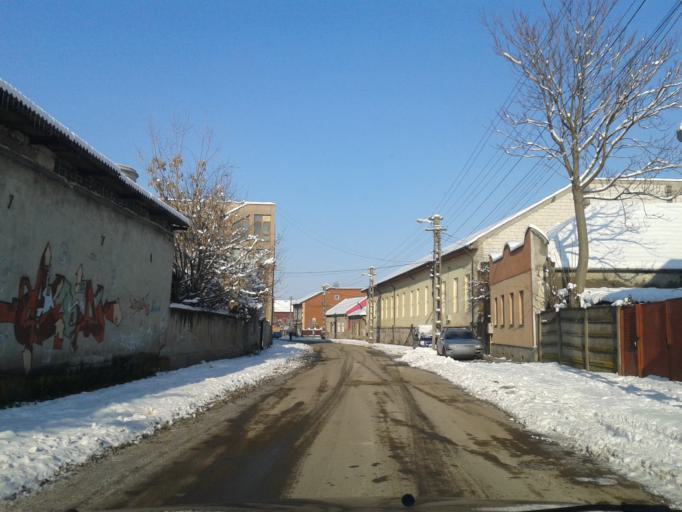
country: RO
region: Hunedoara
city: Hunedoara
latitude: 45.7507
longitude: 22.8906
